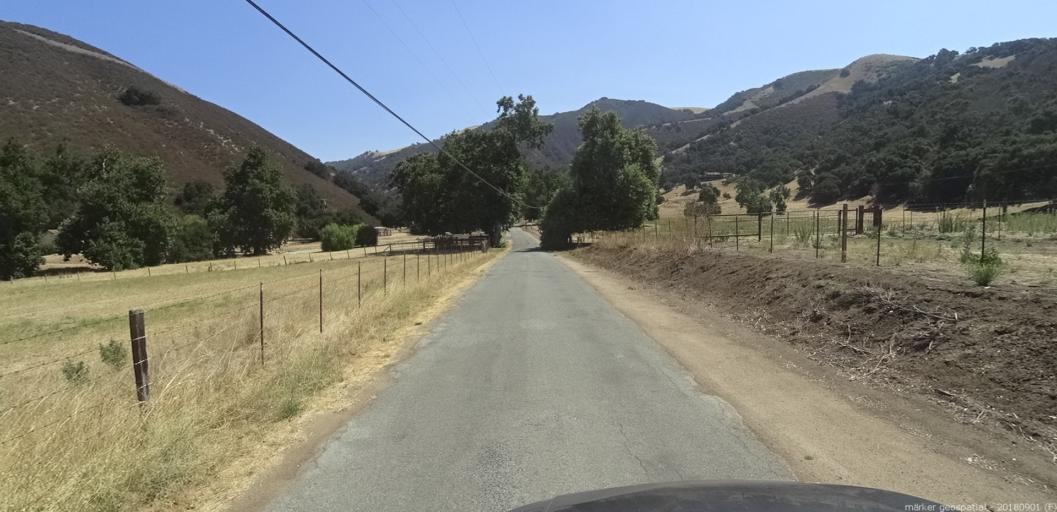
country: US
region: California
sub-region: Monterey County
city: Gonzales
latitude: 36.6037
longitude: -121.4075
